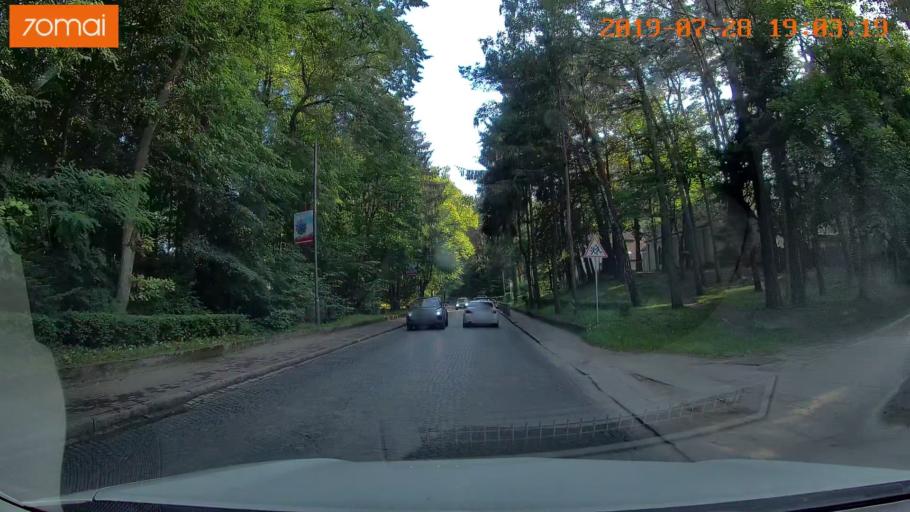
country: RU
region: Kaliningrad
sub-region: Gorod Svetlogorsk
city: Svetlogorsk
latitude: 54.9361
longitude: 20.1624
